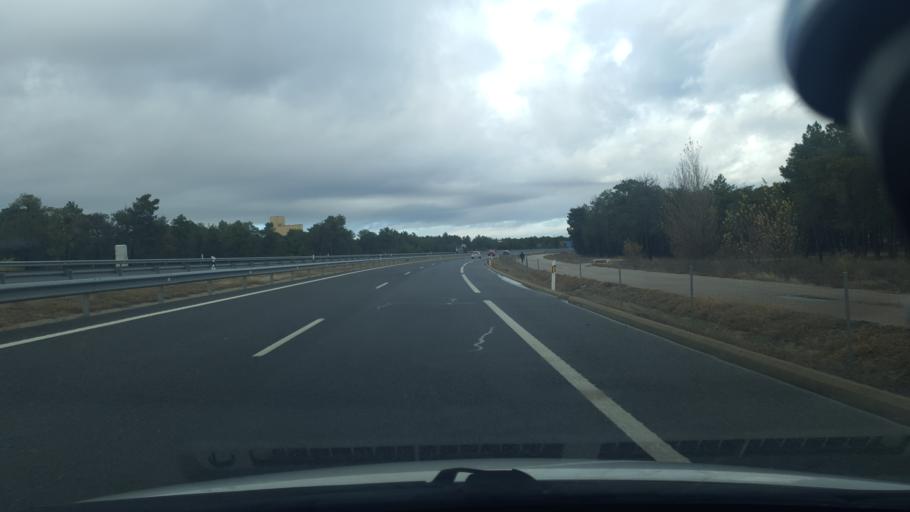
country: ES
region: Castille and Leon
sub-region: Provincia de Segovia
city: Sanchonuno
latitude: 41.3284
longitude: -4.3132
